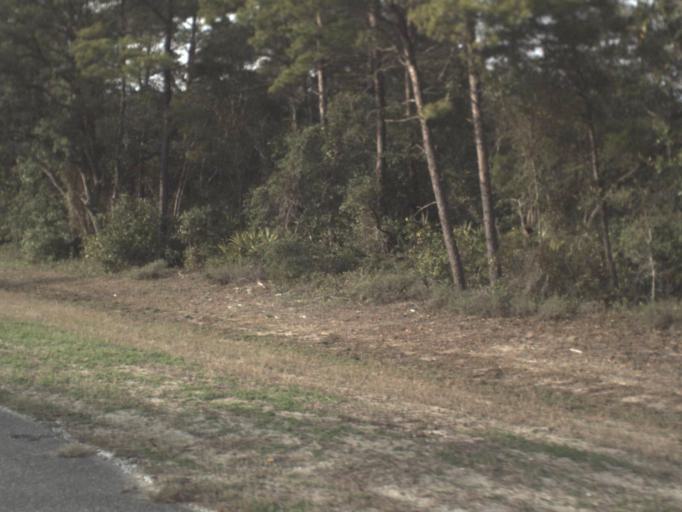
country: US
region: Florida
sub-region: Bay County
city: Mexico Beach
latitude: 29.9585
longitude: -85.4358
